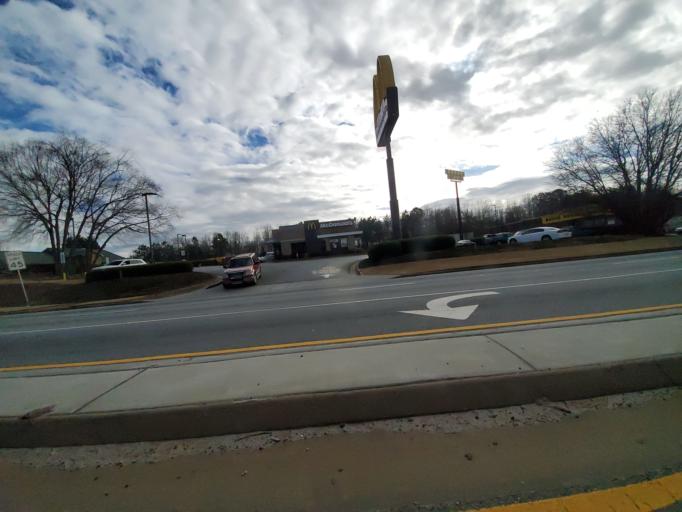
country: US
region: Georgia
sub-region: Jackson County
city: Jefferson
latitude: 34.1522
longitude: -83.6428
